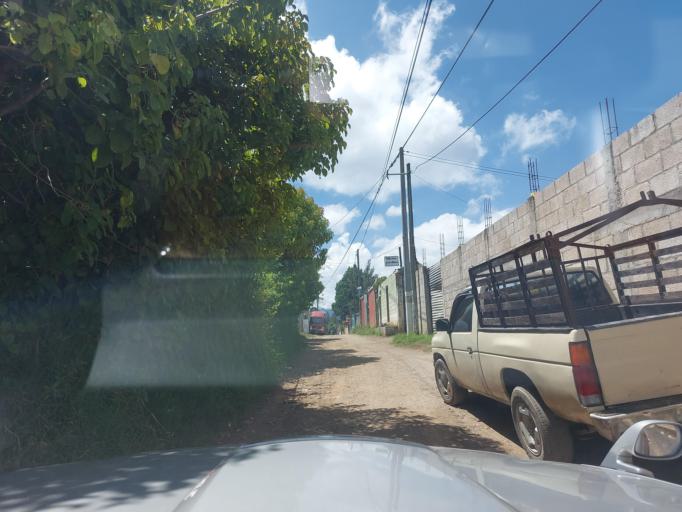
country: GT
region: Chimaltenango
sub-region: Municipio de Chimaltenango
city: Chimaltenango
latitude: 14.6431
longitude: -90.8129
